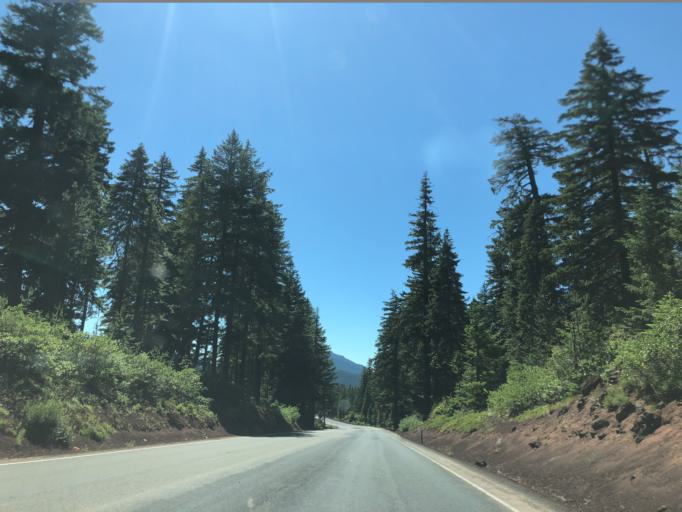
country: US
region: Oregon
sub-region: Deschutes County
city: Sisters
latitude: 44.4328
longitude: -121.9644
